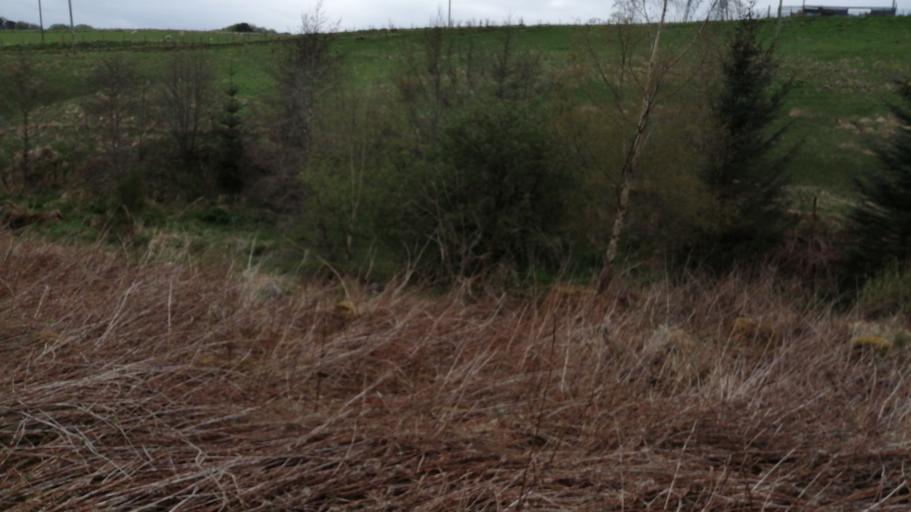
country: GB
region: Scotland
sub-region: Moray
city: Keith
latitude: 57.5346
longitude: -2.9341
